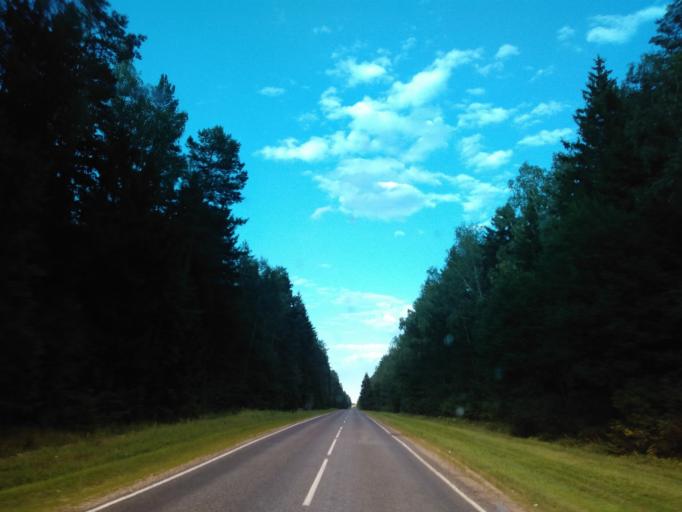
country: BY
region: Minsk
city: Uzda
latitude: 53.4274
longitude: 27.4509
